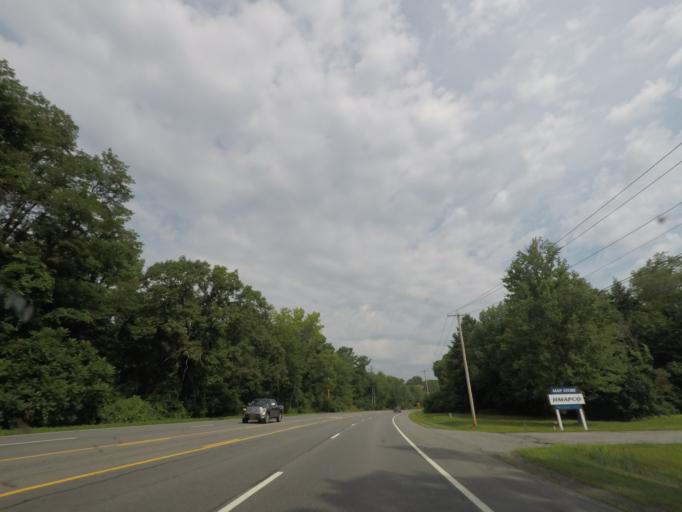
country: US
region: New York
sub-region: Saratoga County
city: Country Knolls
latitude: 42.9227
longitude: -73.7919
